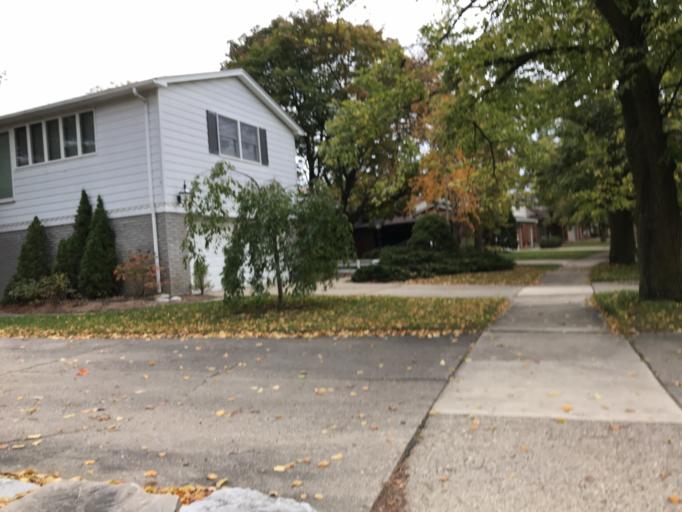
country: US
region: Michigan
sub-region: Washtenaw County
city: Ann Arbor
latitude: 42.2507
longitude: -83.7268
